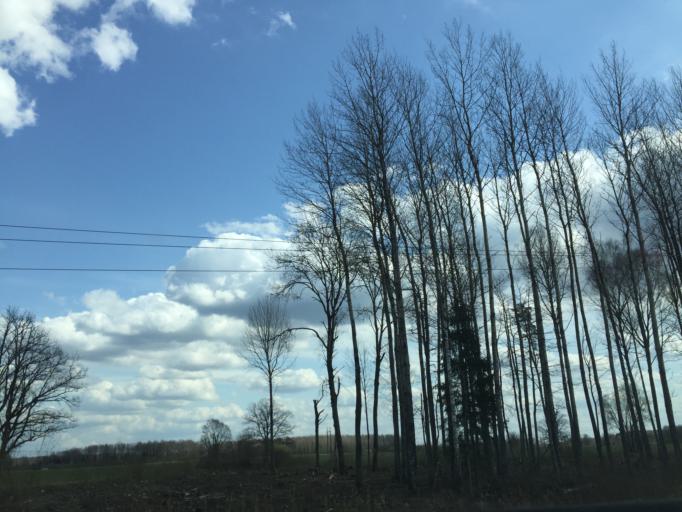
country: LV
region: Skriveri
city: Skriveri
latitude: 56.7557
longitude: 25.1701
